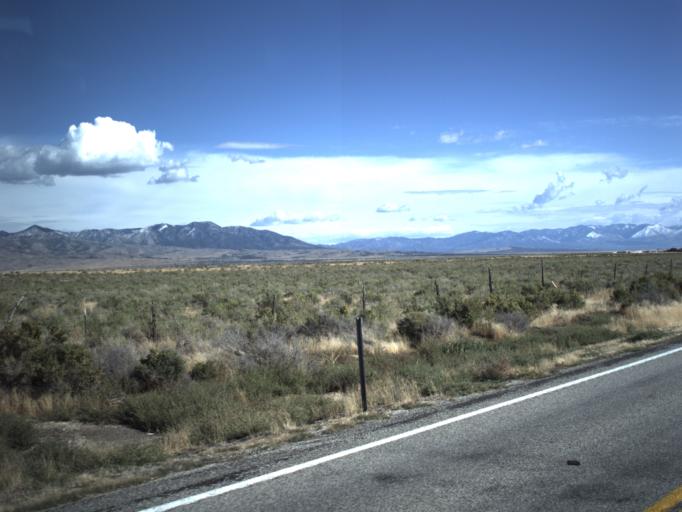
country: US
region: Utah
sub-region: Millard County
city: Delta
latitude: 39.3469
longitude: -112.4954
